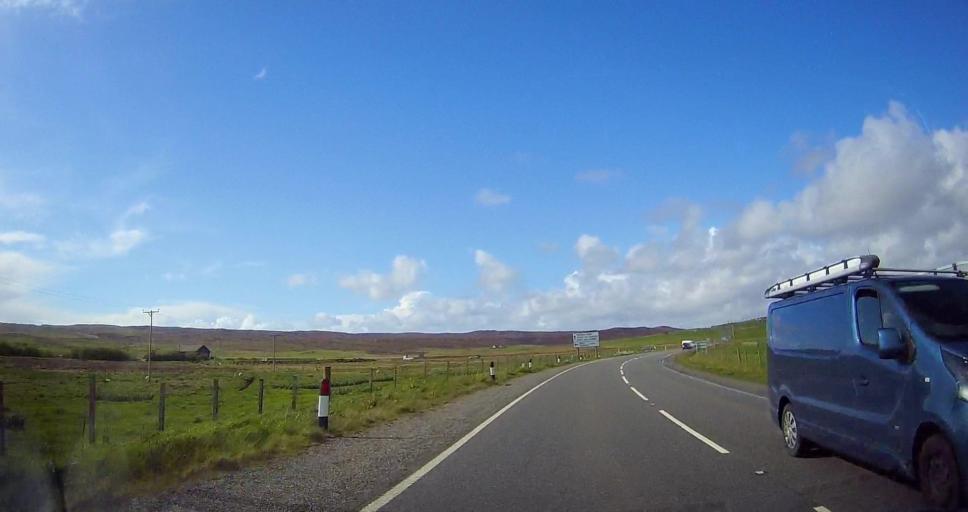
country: GB
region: Scotland
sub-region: Shetland Islands
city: Lerwick
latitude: 60.1886
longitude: -1.2313
